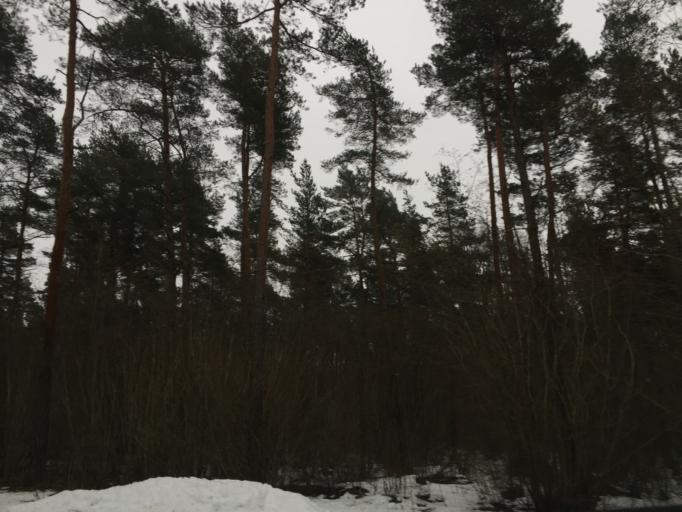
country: EE
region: Saare
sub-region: Kuressaare linn
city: Kuressaare
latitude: 58.2669
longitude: 22.5384
